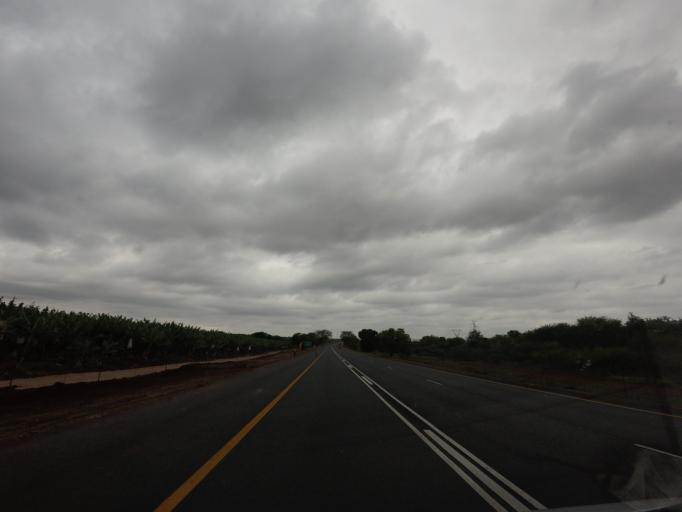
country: ZA
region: Mpumalanga
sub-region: Ehlanzeni District
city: Komatipoort
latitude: -25.4358
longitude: 31.8158
